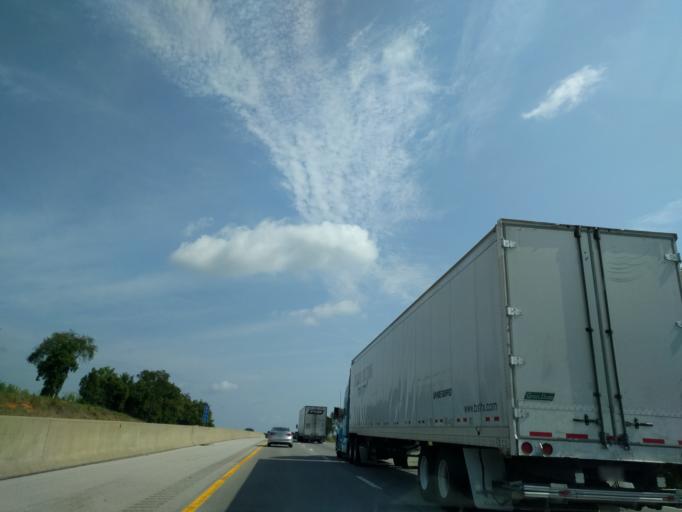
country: US
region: Kentucky
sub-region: Warren County
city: Plano
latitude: 36.7828
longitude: -86.4773
